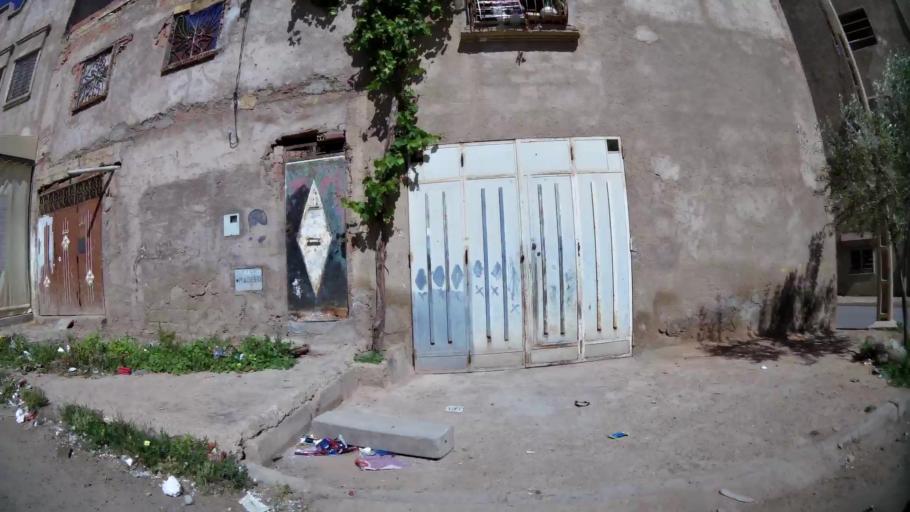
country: MA
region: Oriental
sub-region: Oujda-Angad
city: Oujda
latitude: 34.6570
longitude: -1.9378
